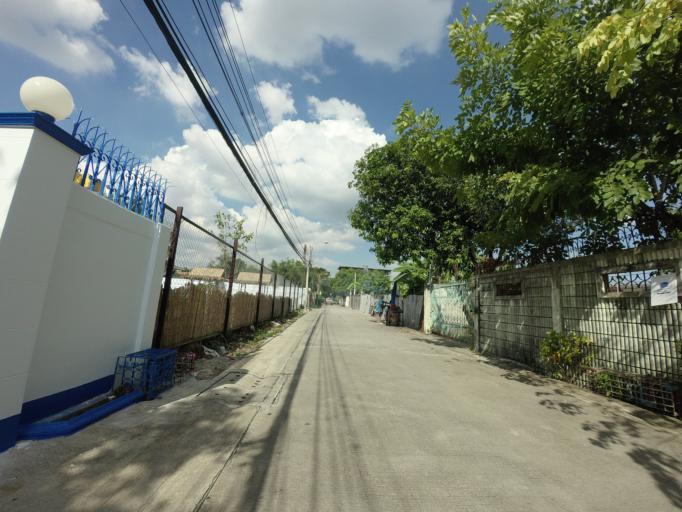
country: TH
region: Bangkok
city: Wang Thonglang
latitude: 13.7875
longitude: 100.5977
